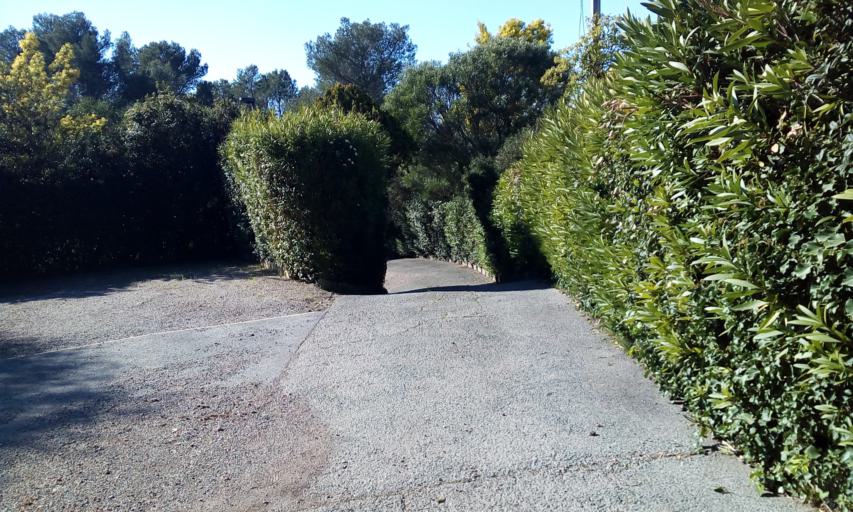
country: FR
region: Provence-Alpes-Cote d'Azur
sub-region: Departement du Var
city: Saint-Raphael
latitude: 43.4452
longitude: 6.7677
